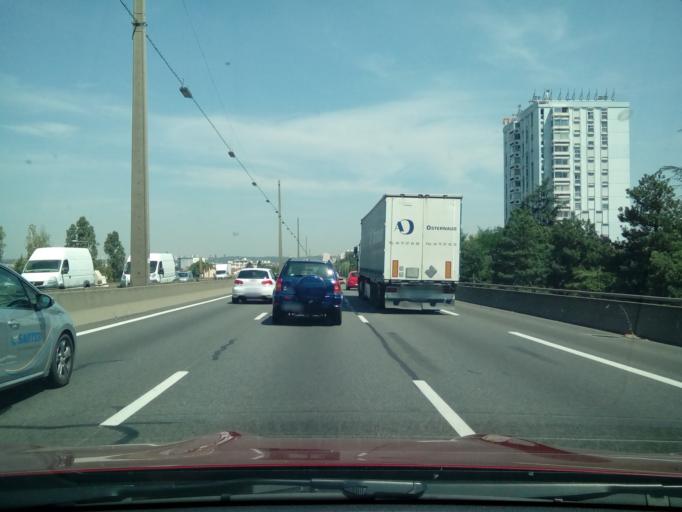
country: FR
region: Rhone-Alpes
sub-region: Departement du Rhone
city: Bron
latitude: 45.7488
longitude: 4.9072
